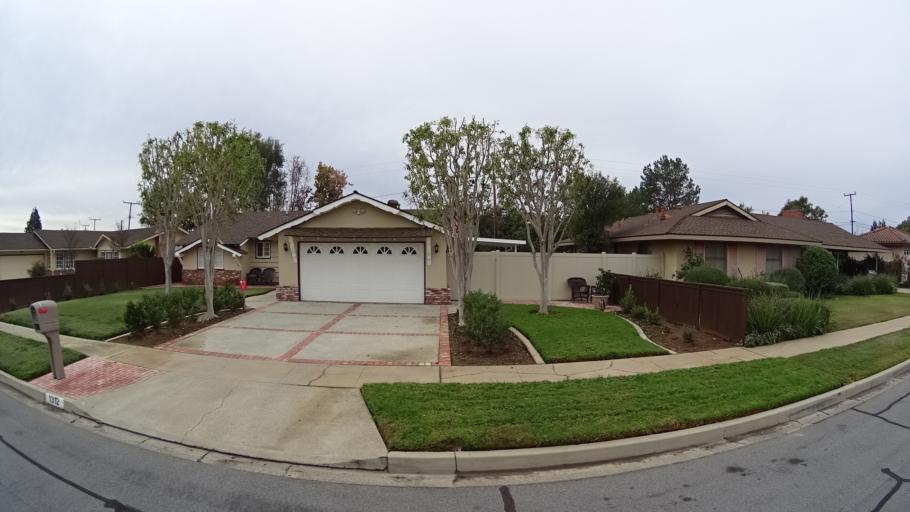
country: US
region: California
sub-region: Orange County
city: North Tustin
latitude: 33.7507
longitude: -117.8025
